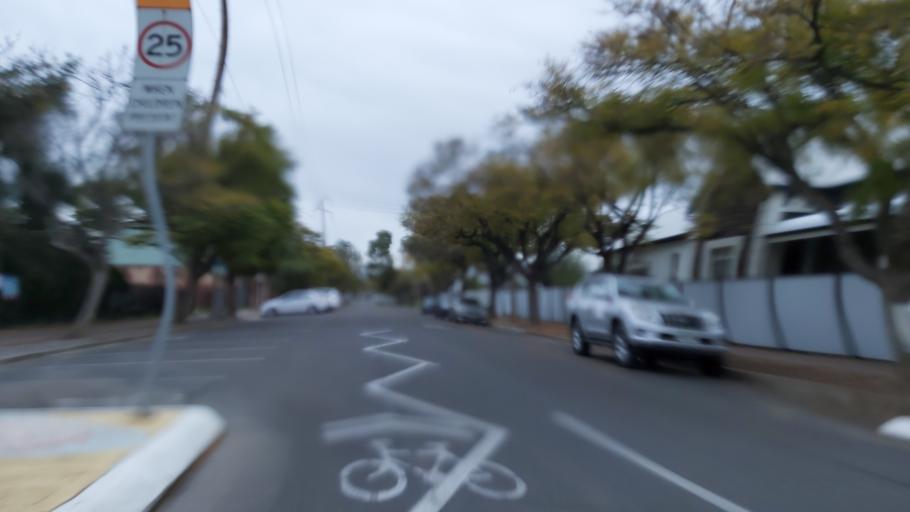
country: AU
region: South Australia
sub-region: Unley
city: Unley
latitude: -34.9503
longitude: 138.6096
